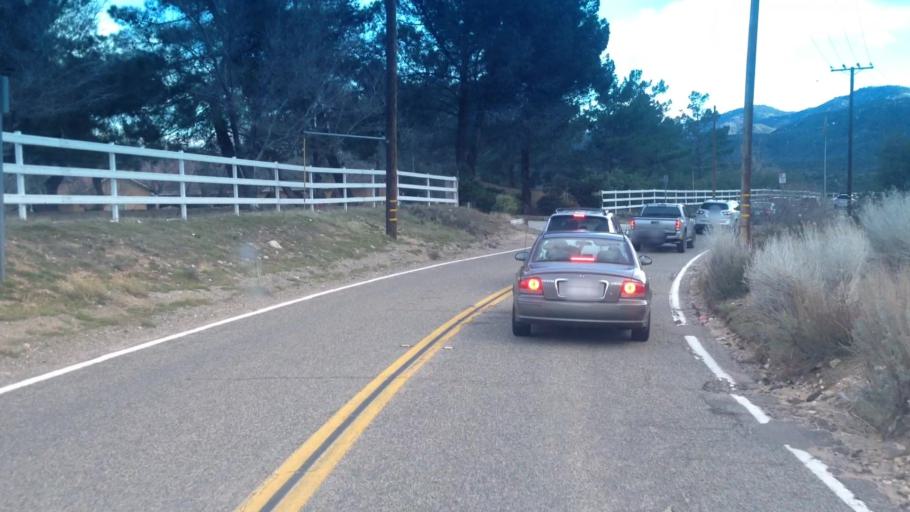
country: US
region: California
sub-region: San Bernardino County
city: Oak Hills
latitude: 34.3321
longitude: -117.3979
